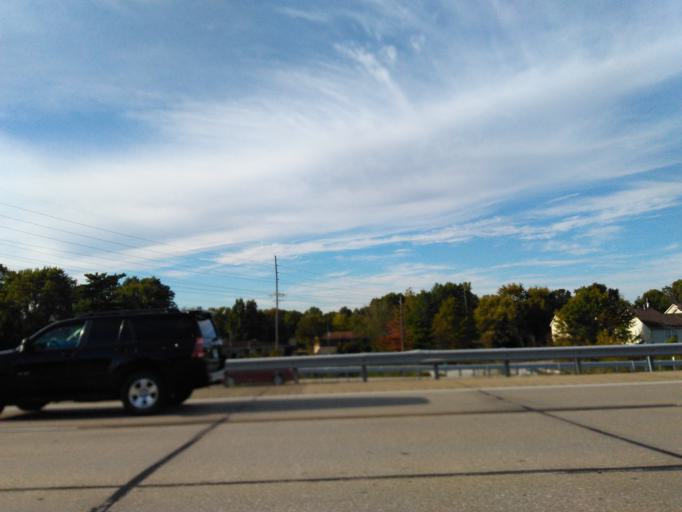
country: US
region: Missouri
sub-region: Saint Louis County
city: Mehlville
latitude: 38.4975
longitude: -90.3083
